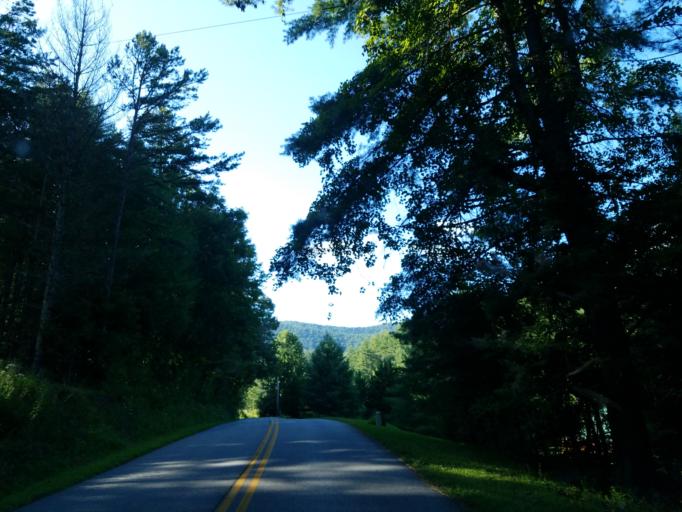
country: US
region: Georgia
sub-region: Union County
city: Blairsville
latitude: 34.7526
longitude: -84.1142
